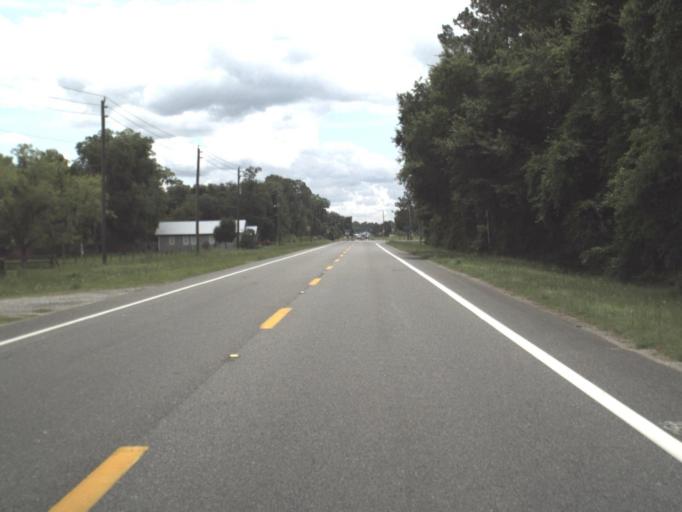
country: US
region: Florida
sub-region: Union County
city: Lake Butler
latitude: 30.0271
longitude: -82.3555
